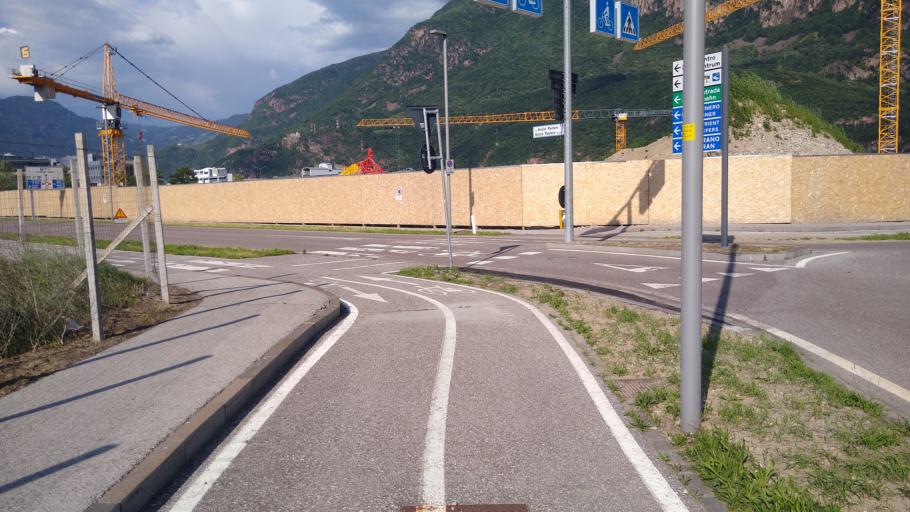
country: IT
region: Trentino-Alto Adige
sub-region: Bolzano
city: San Giacomo
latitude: 46.4676
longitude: 11.3218
